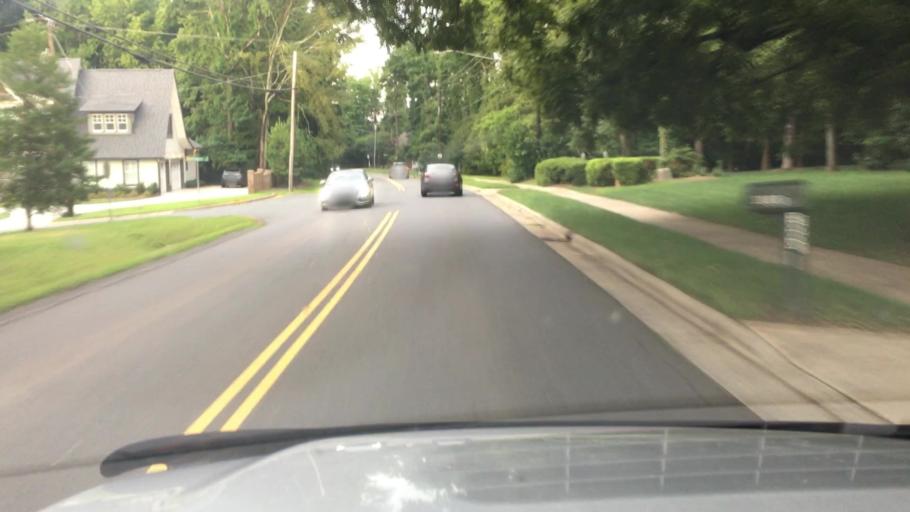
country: US
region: North Carolina
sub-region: Mecklenburg County
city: Pineville
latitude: 35.1280
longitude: -80.8149
